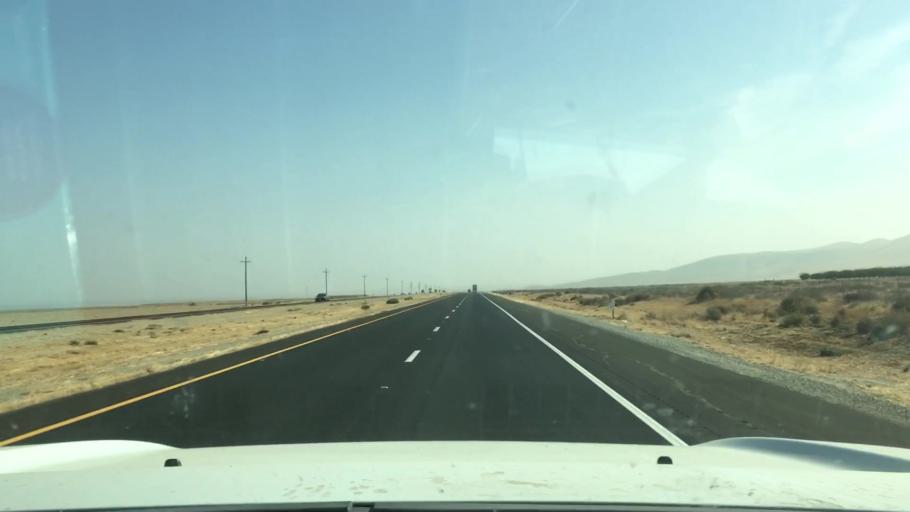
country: US
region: California
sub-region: San Luis Obispo County
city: Shandon
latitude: 35.6697
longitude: -120.0796
